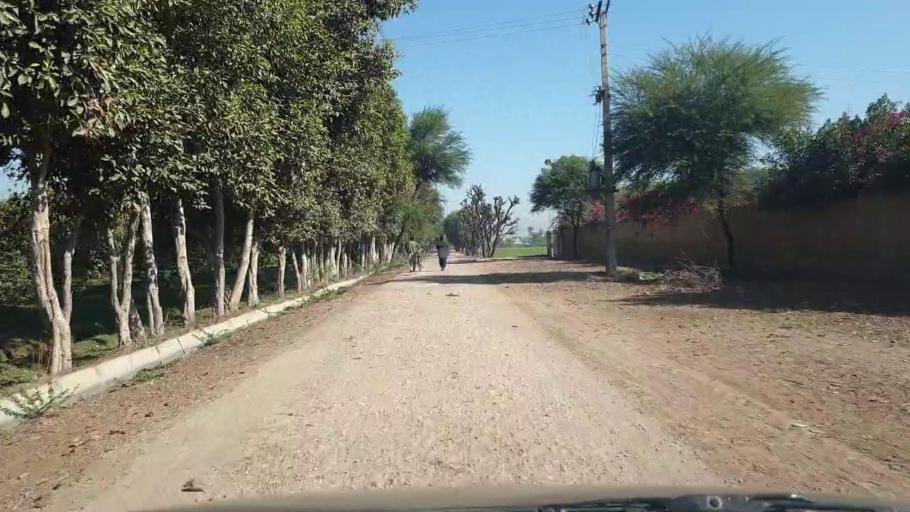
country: PK
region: Sindh
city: Umarkot
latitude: 25.3733
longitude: 69.7013
